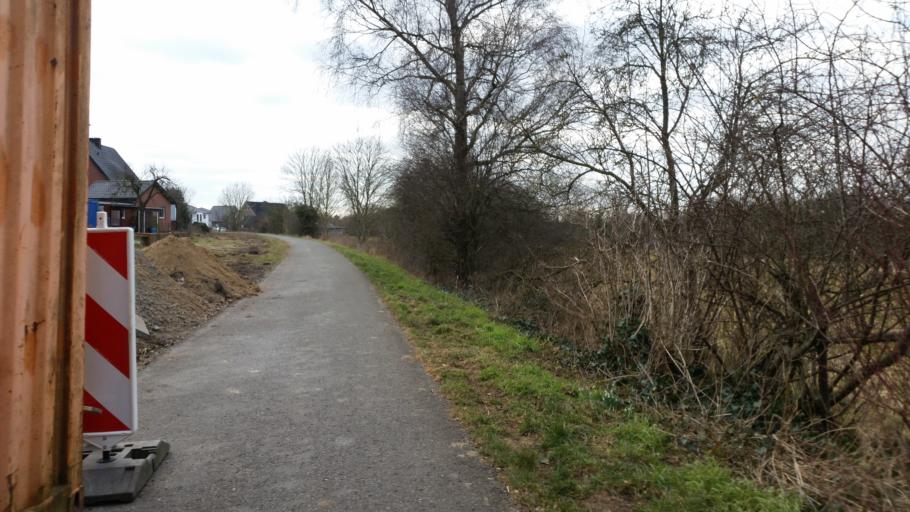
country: DE
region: North Rhine-Westphalia
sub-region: Regierungsbezirk Munster
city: Rheine
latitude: 52.2763
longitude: 7.4057
